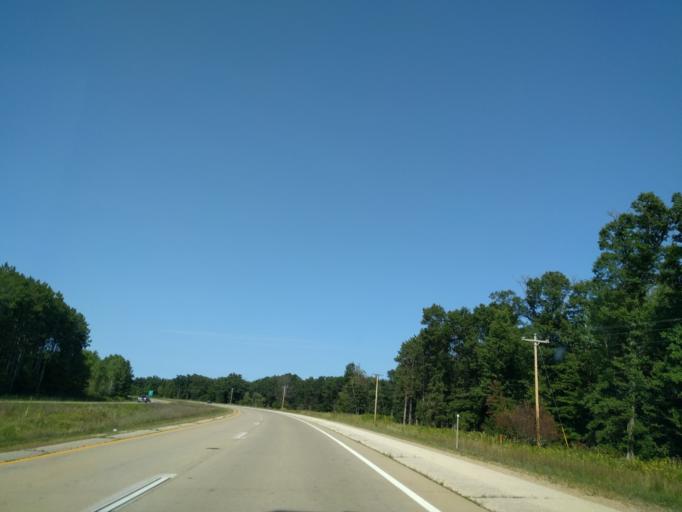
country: US
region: Wisconsin
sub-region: Oconto County
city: Oconto
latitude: 44.8502
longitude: -87.9014
